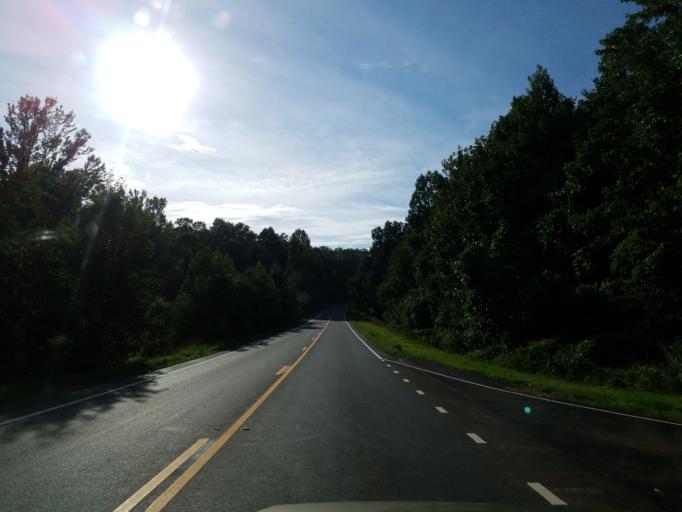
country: US
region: Georgia
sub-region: White County
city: Cleveland
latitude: 34.6313
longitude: -83.8199
